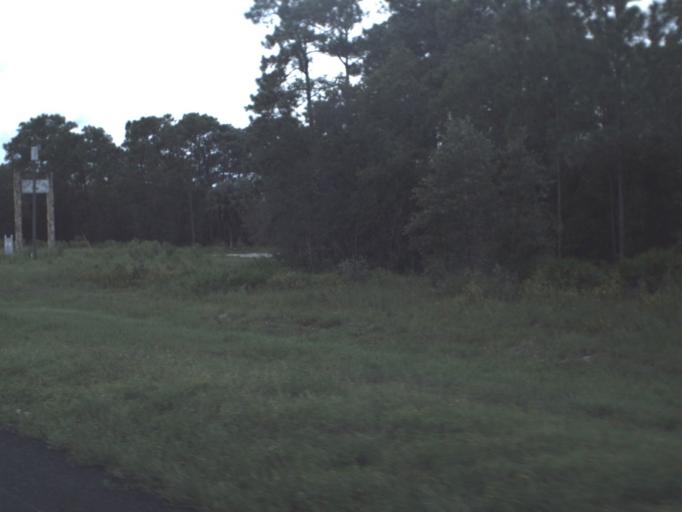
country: US
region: Florida
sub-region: Citrus County
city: Sugarmill Woods
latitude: 28.6837
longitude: -82.5526
